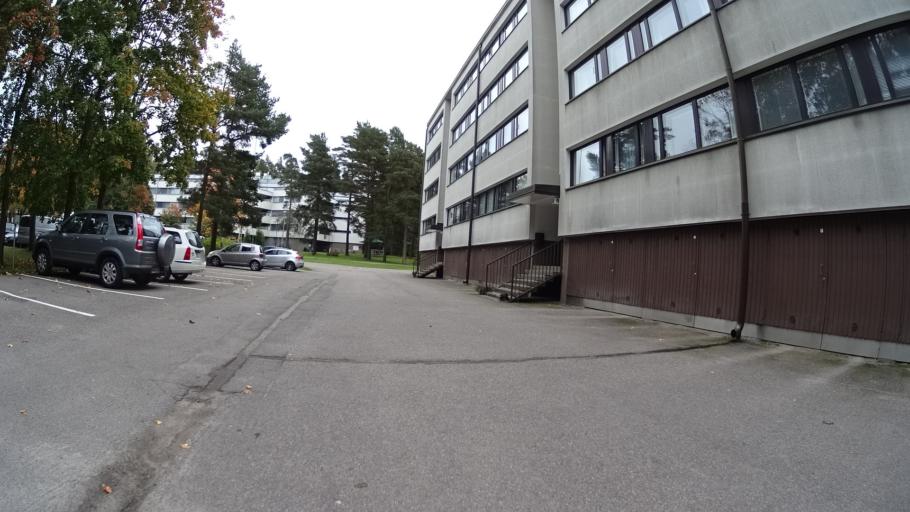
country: FI
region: Uusimaa
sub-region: Helsinki
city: Vantaa
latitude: 60.2261
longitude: 25.0692
